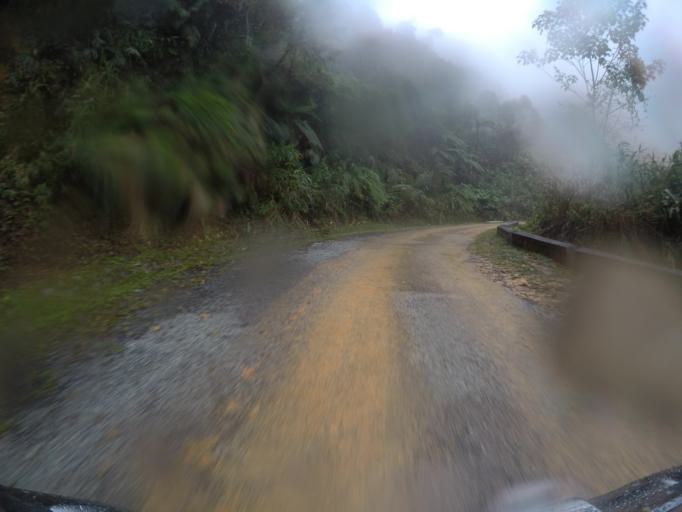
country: LA
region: Xekong
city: Dak Cheung
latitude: 15.5603
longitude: 107.3951
